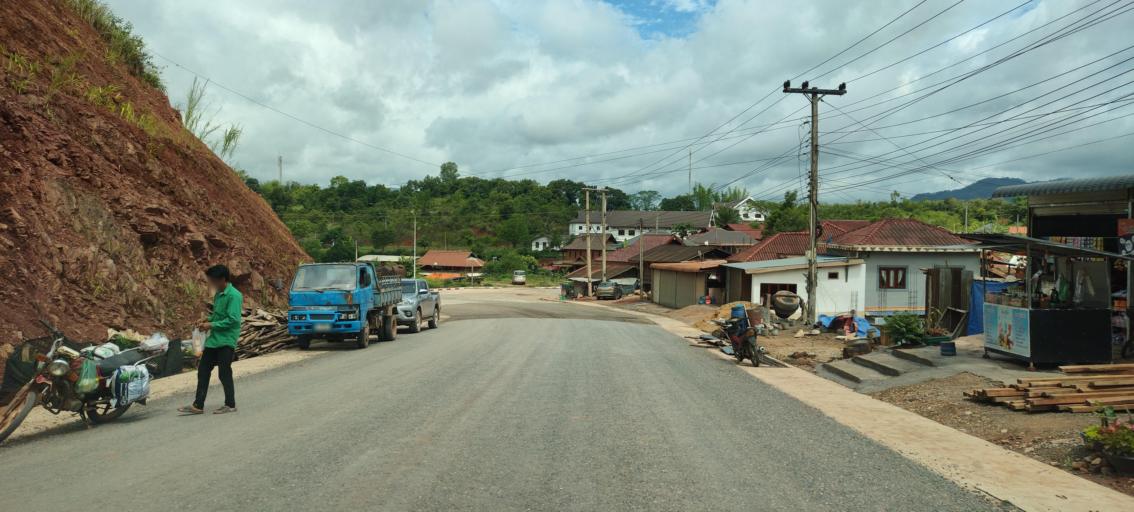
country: LA
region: Phongsali
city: Phongsali
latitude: 21.6382
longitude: 101.9167
